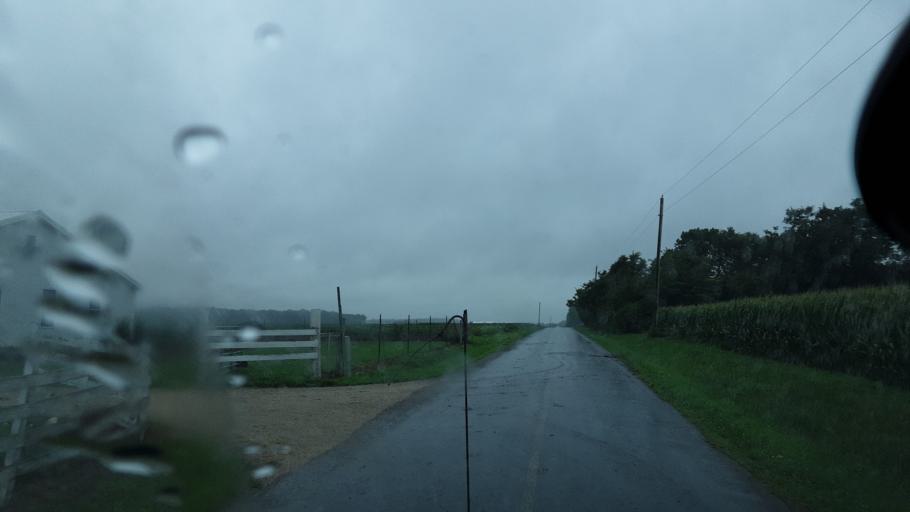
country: US
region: Ohio
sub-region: Mercer County
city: Rockford
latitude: 40.6858
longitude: -84.7948
